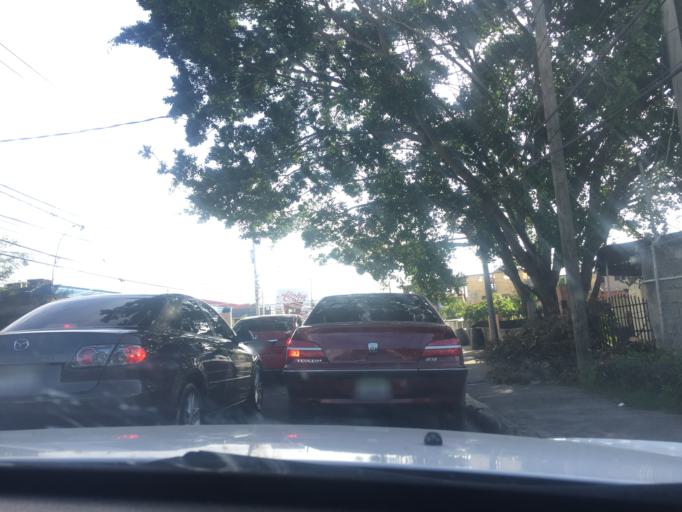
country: DO
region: Santiago
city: Santiago de los Caballeros
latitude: 19.4672
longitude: -70.6580
